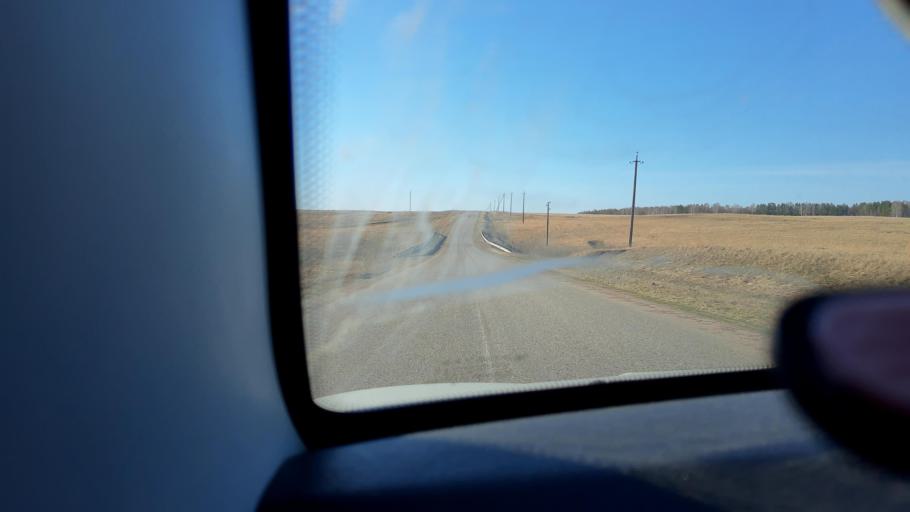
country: RU
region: Bashkortostan
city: Asanovo
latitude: 54.8140
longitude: 55.4803
